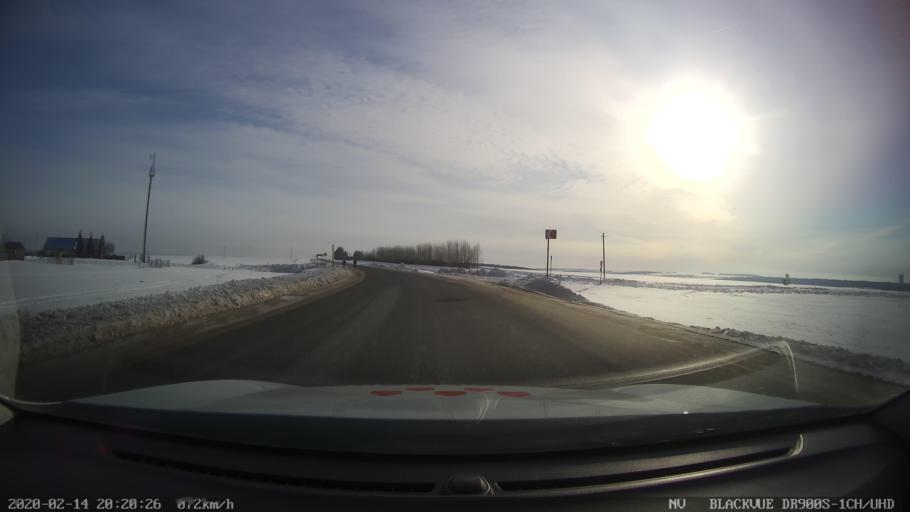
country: RU
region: Tatarstan
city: Verkhniy Uslon
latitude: 55.5572
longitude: 48.9062
